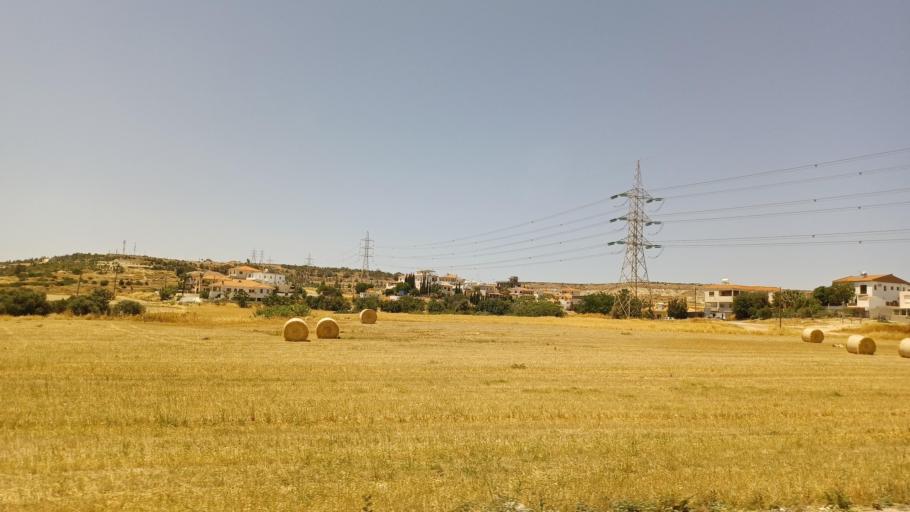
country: CY
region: Larnaka
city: Pyla
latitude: 35.0033
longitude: 33.6885
